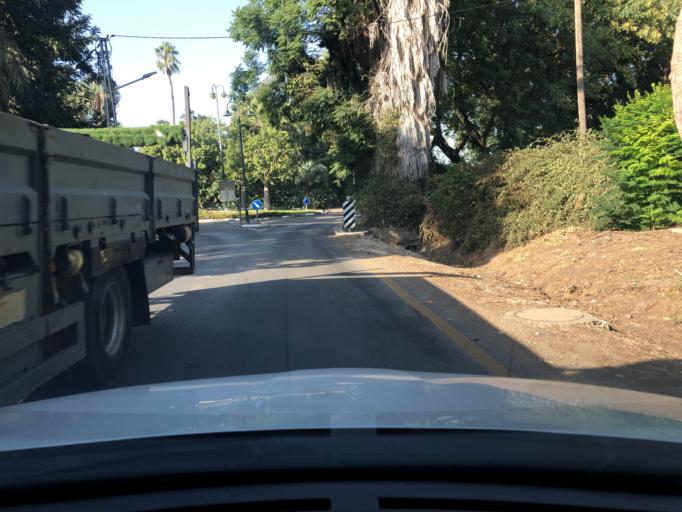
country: IL
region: Central District
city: Hod HaSharon
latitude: 32.1387
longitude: 34.9079
